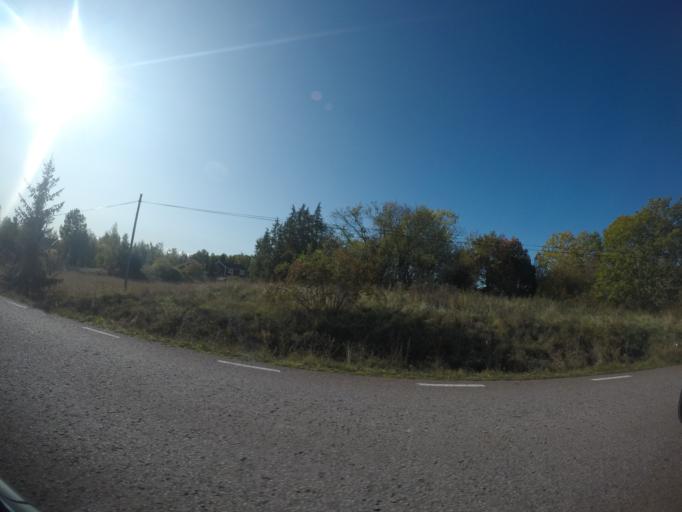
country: SE
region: Soedermanland
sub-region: Eskilstuna Kommun
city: Kvicksund
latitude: 59.5584
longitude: 16.4094
